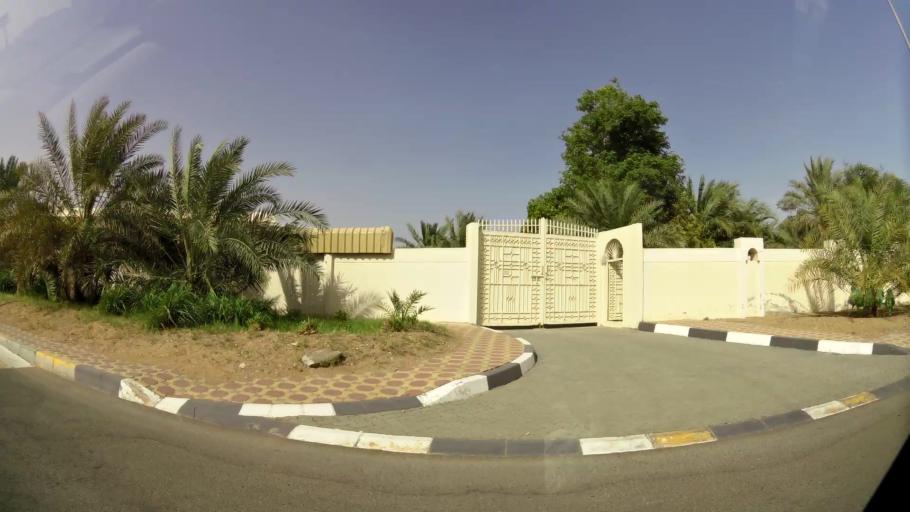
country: AE
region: Abu Dhabi
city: Al Ain
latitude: 24.2426
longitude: 55.6814
